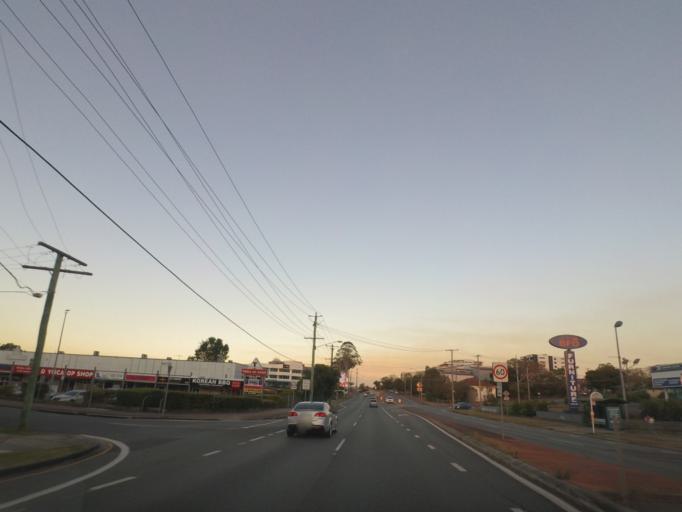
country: AU
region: Queensland
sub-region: Brisbane
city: Upper Mount Gravatt
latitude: -27.5591
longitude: 153.0832
